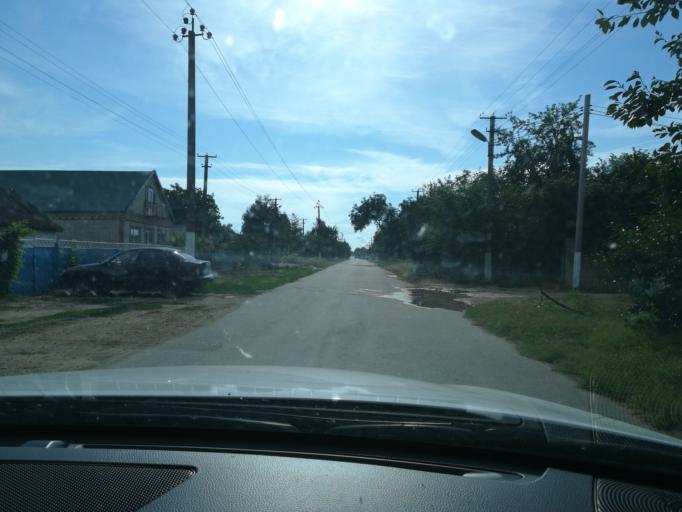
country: RU
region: Krasnodarskiy
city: Strelka
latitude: 45.1729
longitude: 37.2740
